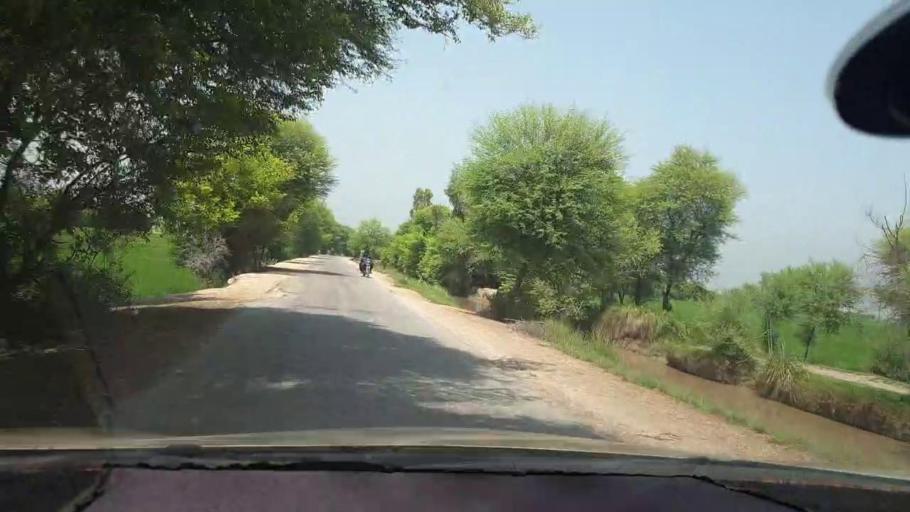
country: PK
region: Sindh
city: Kambar
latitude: 27.6465
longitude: 67.9704
